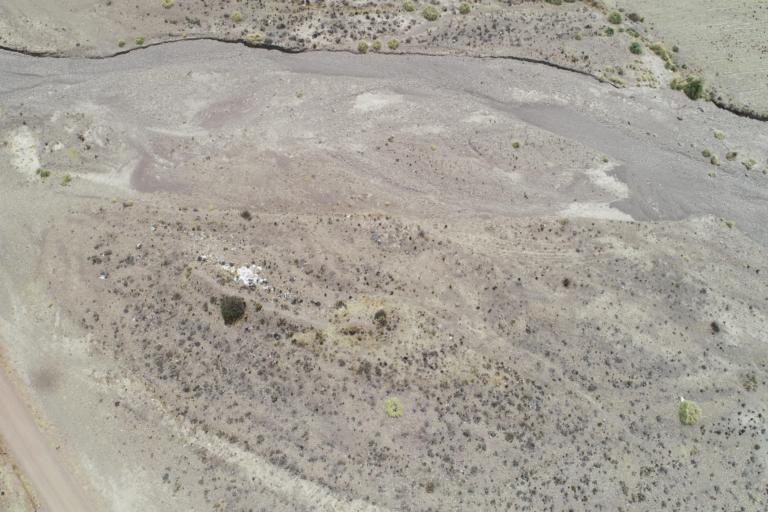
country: BO
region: La Paz
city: Achacachi
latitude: -15.9101
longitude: -68.8830
